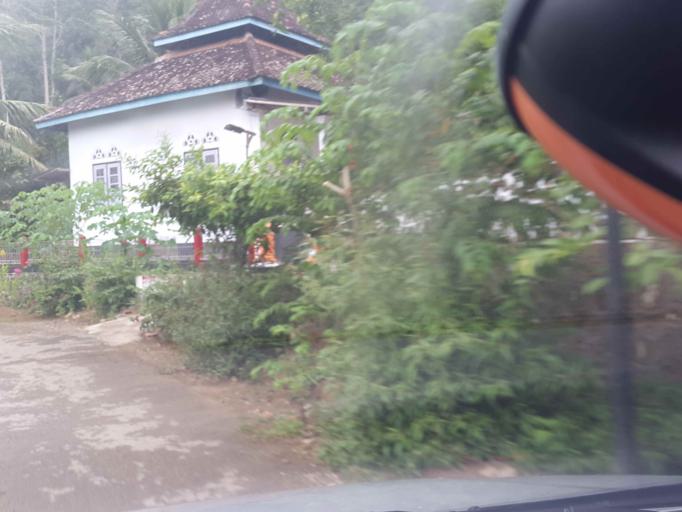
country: ID
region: East Java
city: Sudimoro
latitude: -8.2004
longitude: 111.3326
